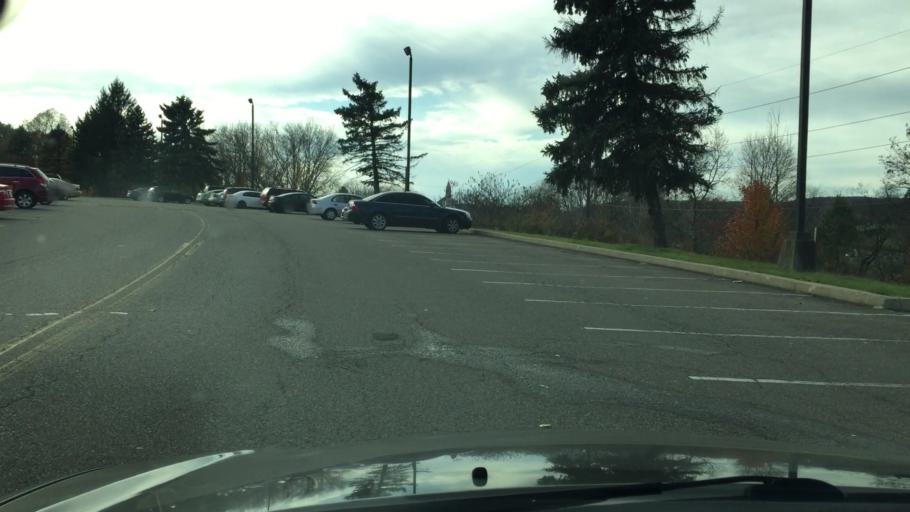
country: US
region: Pennsylvania
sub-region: Luzerne County
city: Nanticoke
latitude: 41.1962
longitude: -75.9919
